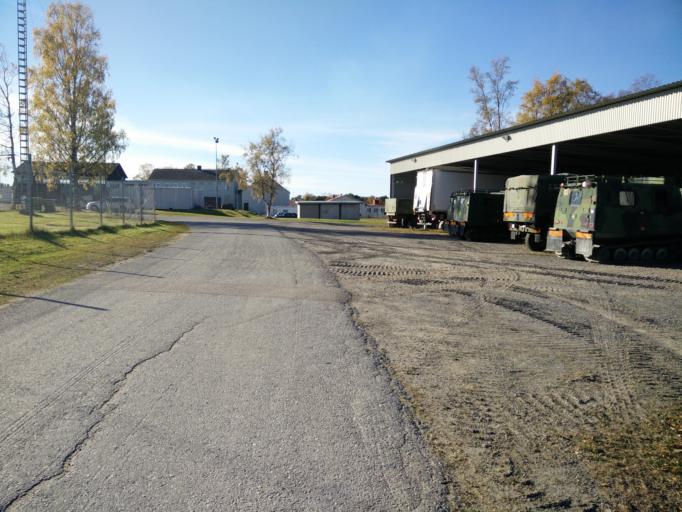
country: SE
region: Vaesternorrland
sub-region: Haernoesands Kommun
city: Haernoesand
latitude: 62.6406
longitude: 17.9650
